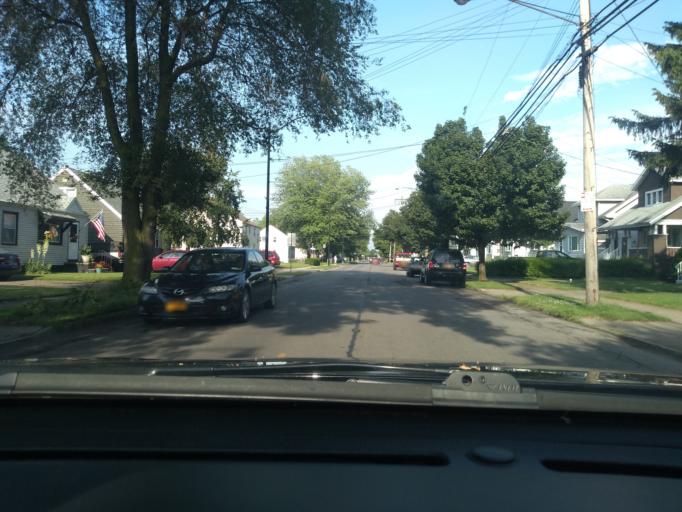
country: US
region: New York
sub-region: Erie County
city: Lackawanna
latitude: 42.8470
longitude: -78.8290
